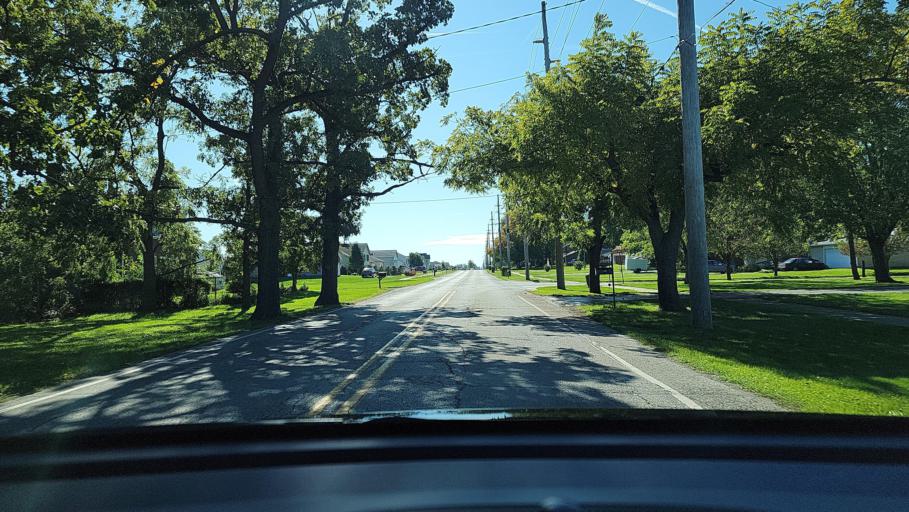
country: US
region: Indiana
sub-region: Porter County
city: Portage
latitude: 41.5688
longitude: -87.1636
